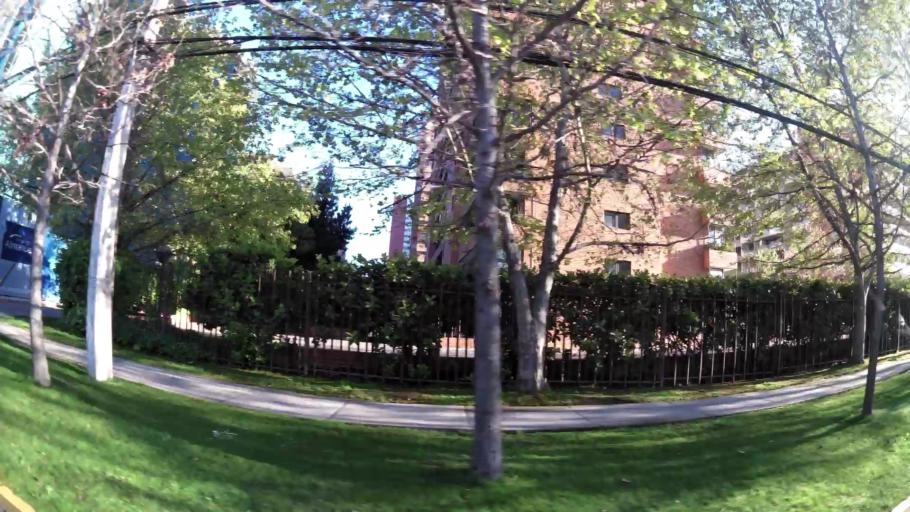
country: CL
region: Santiago Metropolitan
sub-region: Provincia de Santiago
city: Villa Presidente Frei, Nunoa, Santiago, Chile
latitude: -33.3982
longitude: -70.5648
